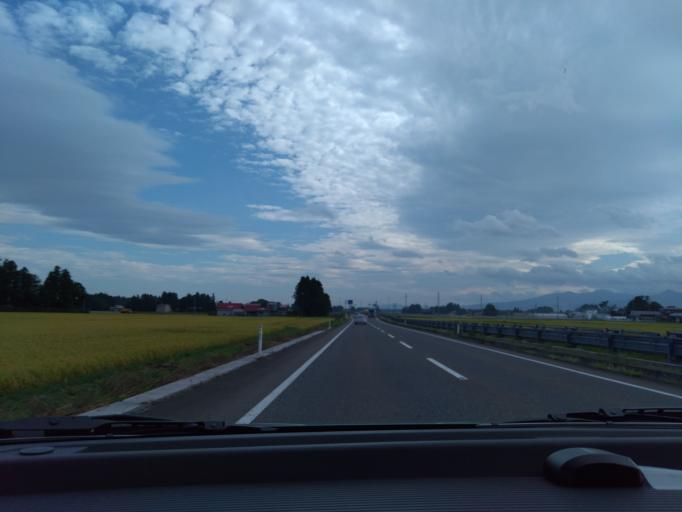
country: JP
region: Iwate
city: Hanamaki
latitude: 39.3596
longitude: 141.0554
